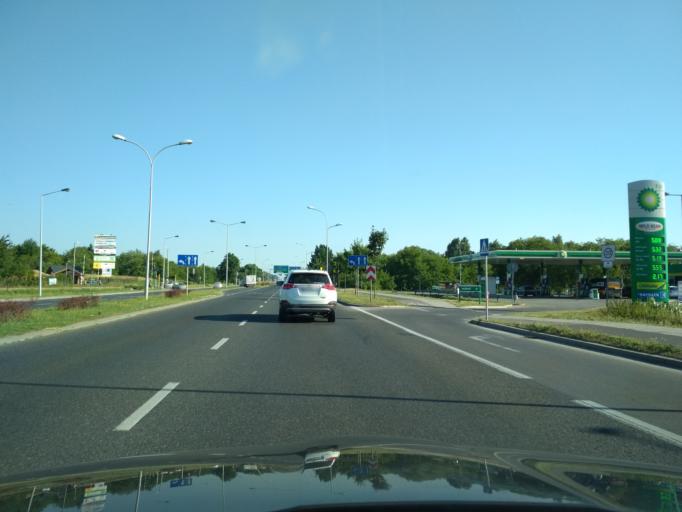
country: PL
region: Subcarpathian Voivodeship
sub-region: Rzeszow
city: Rzeszow
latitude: 50.0625
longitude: 21.9930
